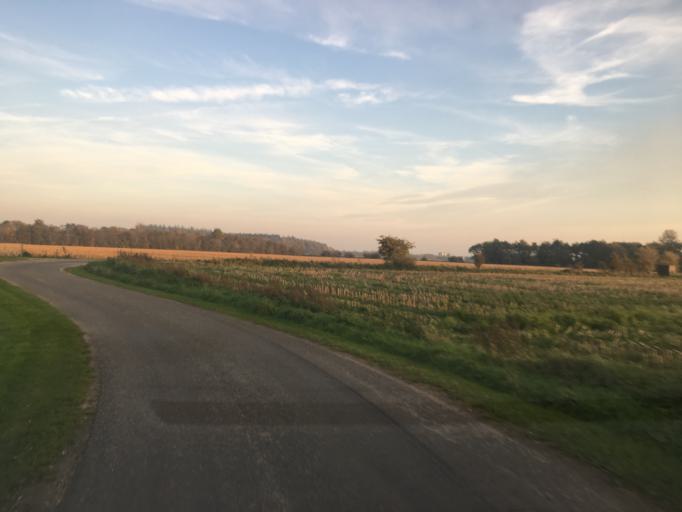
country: DK
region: South Denmark
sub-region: Tonder Kommune
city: Toftlund
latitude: 55.0353
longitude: 9.1163
